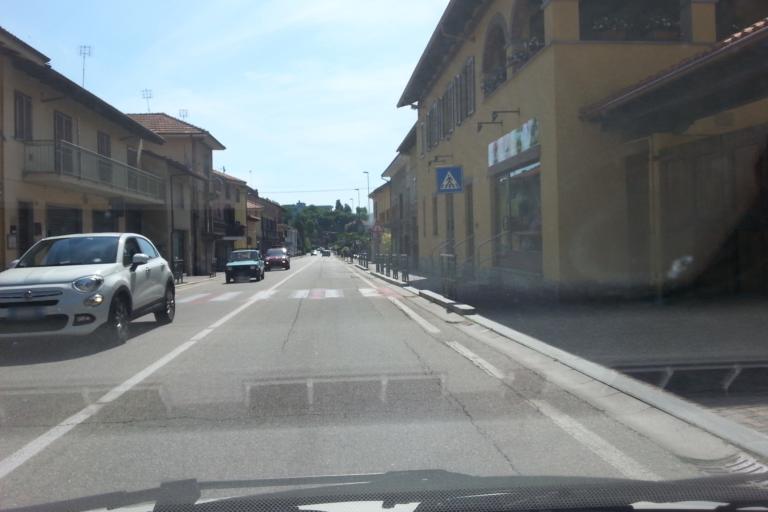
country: IT
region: Piedmont
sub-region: Provincia di Torino
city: Avigliana
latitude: 45.0768
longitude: 7.3979
